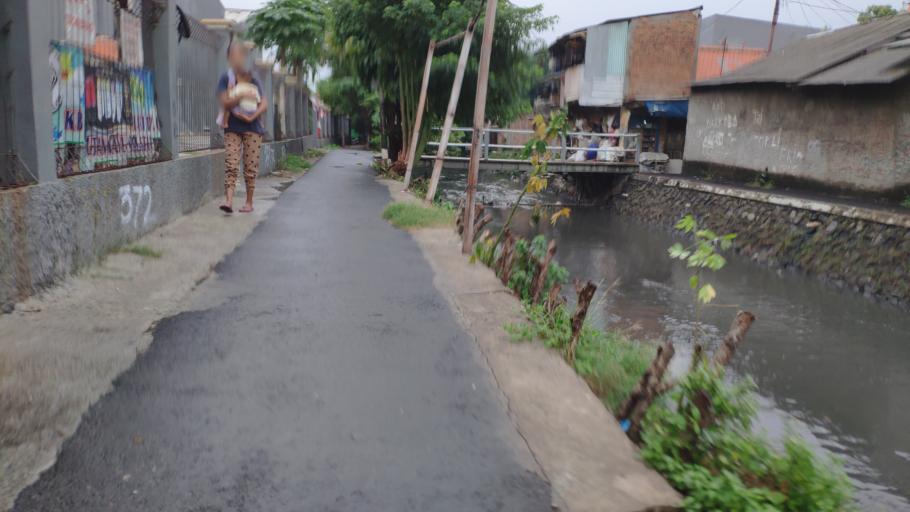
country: ID
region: Jakarta Raya
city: Jakarta
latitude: -6.2051
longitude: 106.8694
